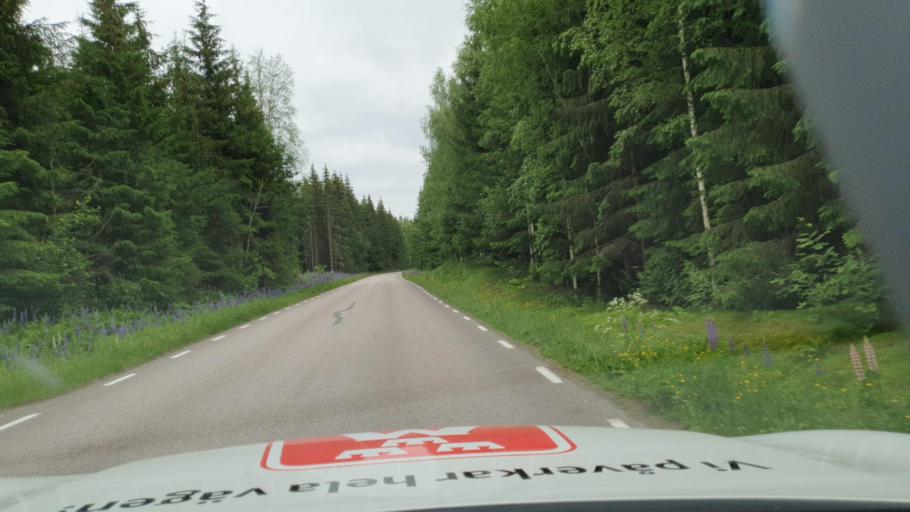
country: SE
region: Vaermland
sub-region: Sunne Kommun
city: Sunne
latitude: 59.7287
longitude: 13.2180
